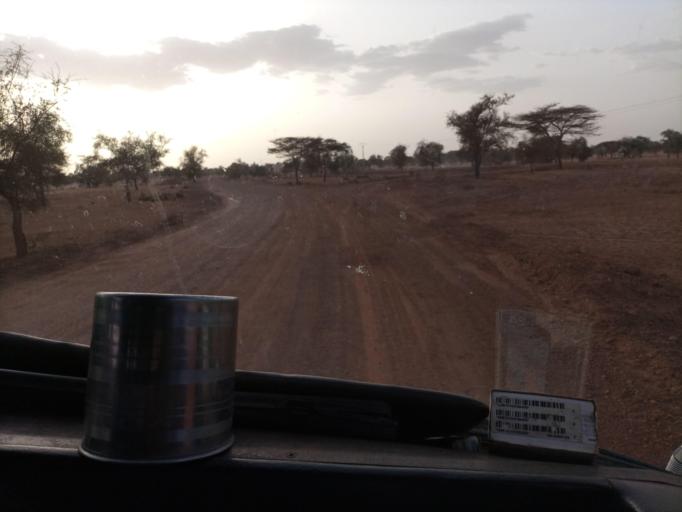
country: SN
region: Louga
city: Dara
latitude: 15.3718
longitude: -15.5821
